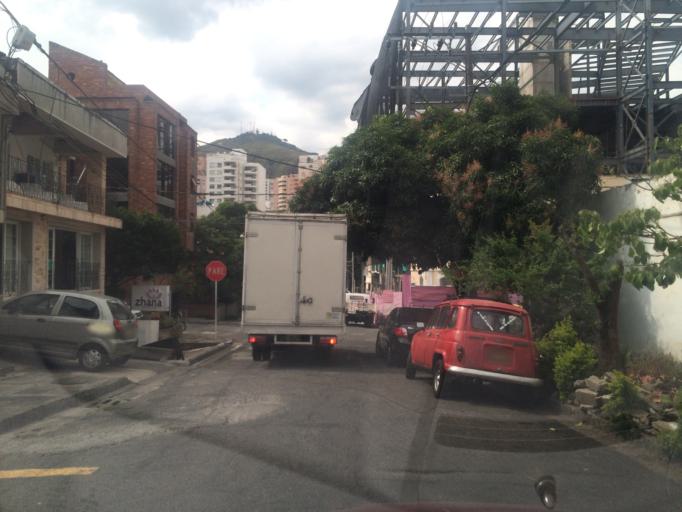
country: CO
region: Valle del Cauca
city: Cali
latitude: 3.4492
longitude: -76.5436
